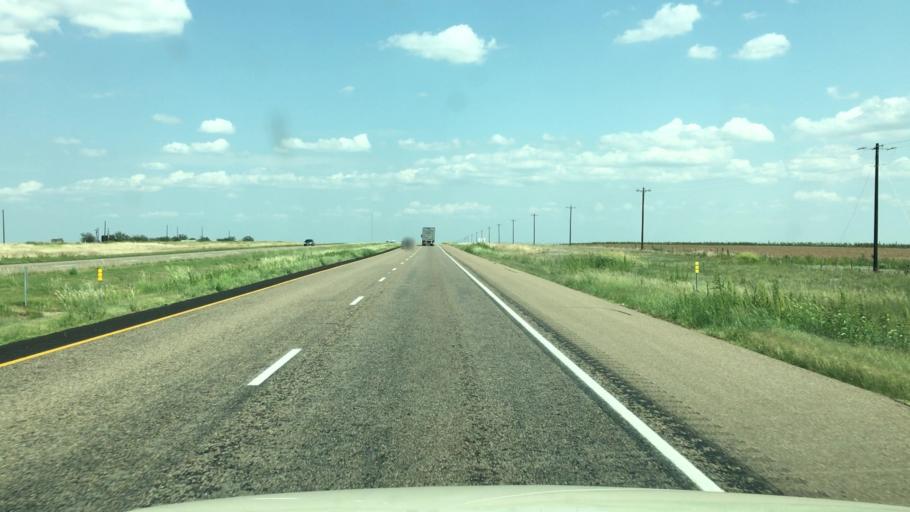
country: US
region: Texas
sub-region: Armstrong County
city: Claude
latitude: 35.0336
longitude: -101.1756
